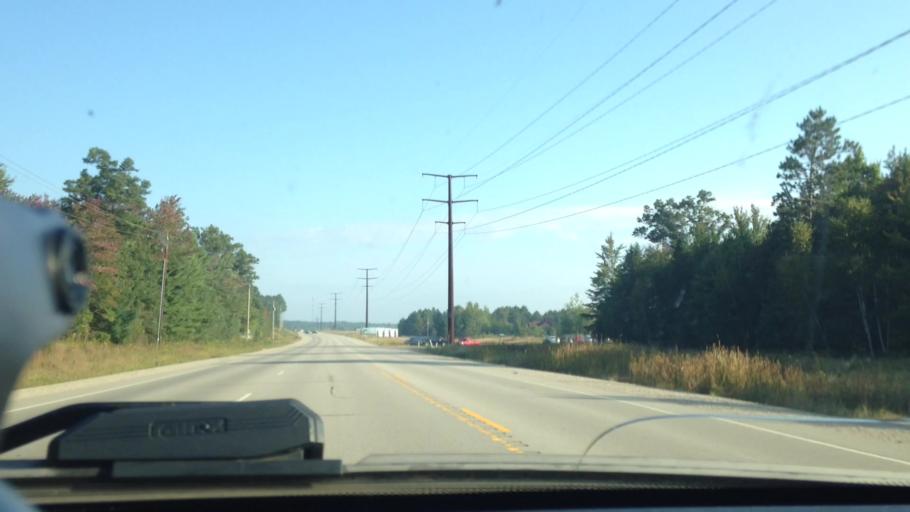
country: US
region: Wisconsin
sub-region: Marinette County
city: Peshtigo
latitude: 45.1945
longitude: -87.9947
